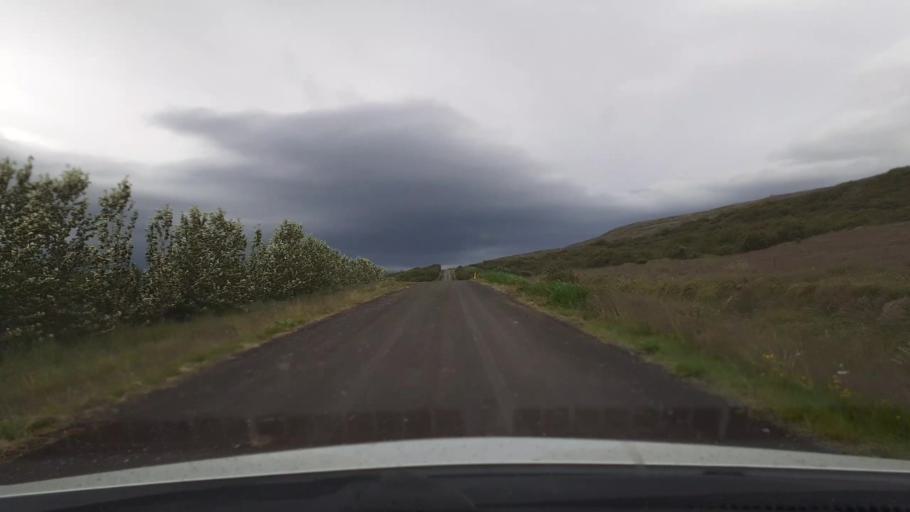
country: IS
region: Capital Region
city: Mosfellsbaer
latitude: 64.5228
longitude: -21.4698
